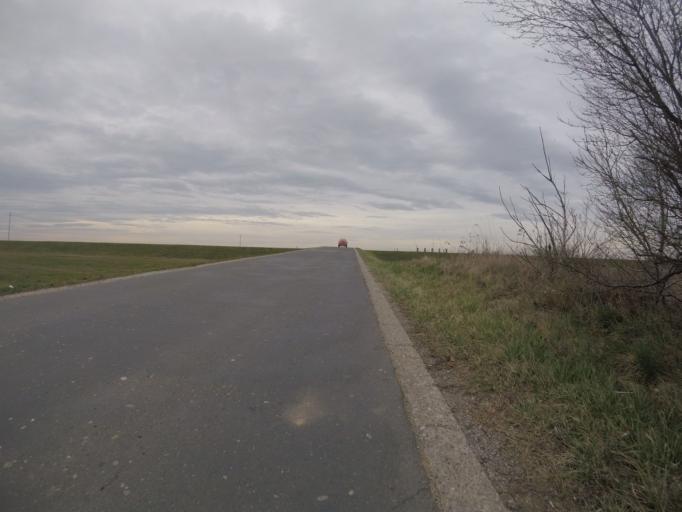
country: HR
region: Zagrebacka
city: Lukavec
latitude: 45.7073
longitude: 16.0117
